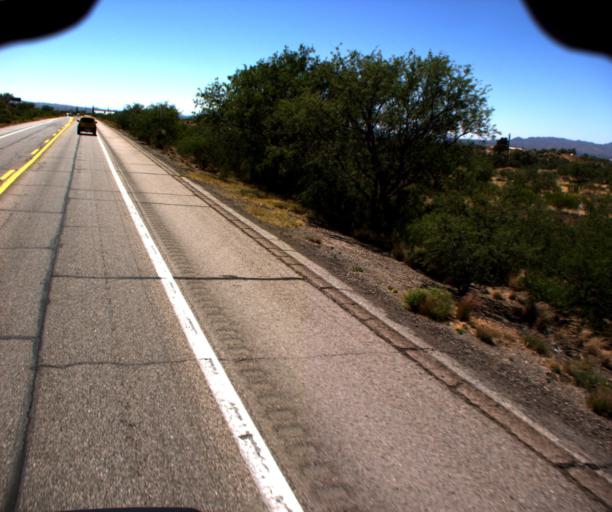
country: US
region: Arizona
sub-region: Pinal County
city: Oracle
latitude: 32.6227
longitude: -110.7880
